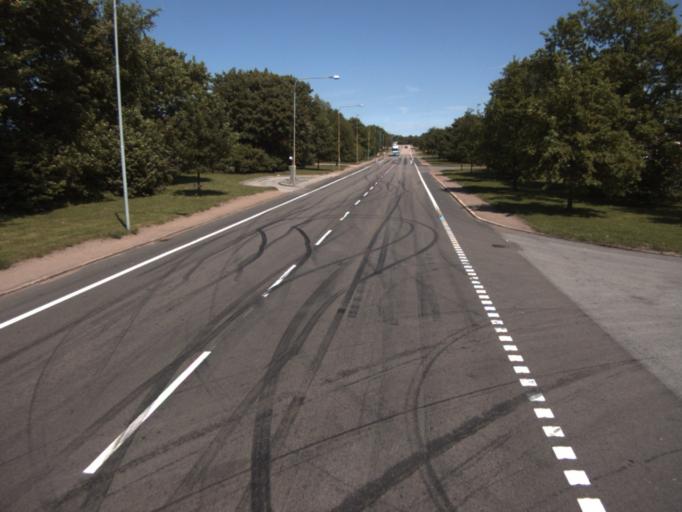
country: SE
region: Skane
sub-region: Helsingborg
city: Gantofta
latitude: 56.0108
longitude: 12.7666
